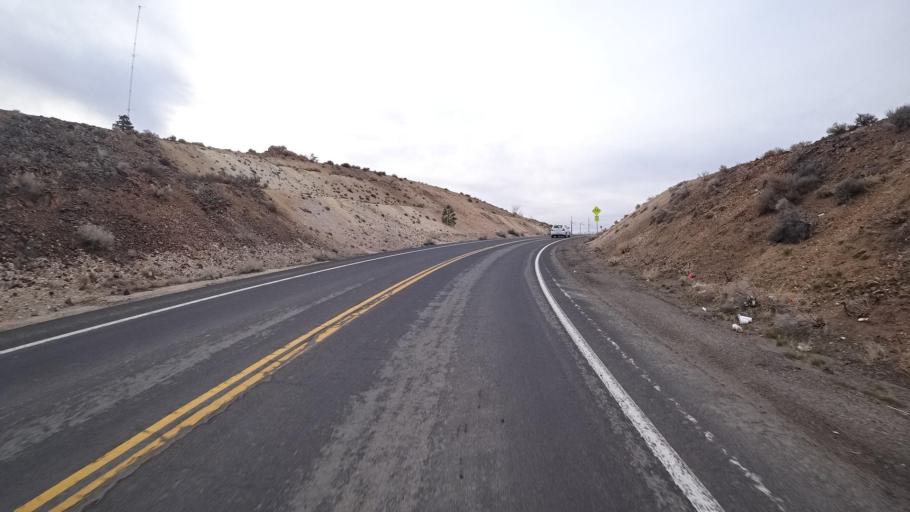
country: US
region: Nevada
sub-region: Washoe County
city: Sun Valley
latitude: 39.5748
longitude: -119.8061
